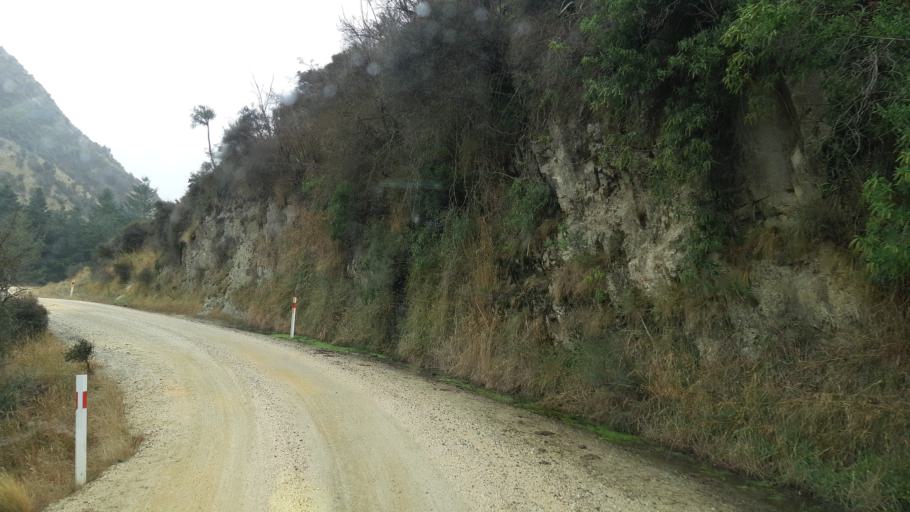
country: NZ
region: Otago
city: Oamaru
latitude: -44.9601
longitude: 170.4596
